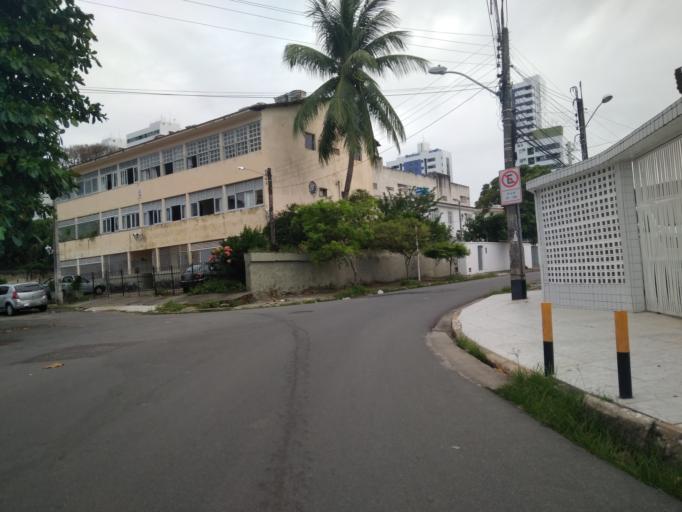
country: BR
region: Pernambuco
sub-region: Recife
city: Recife
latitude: -8.0342
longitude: -34.8884
